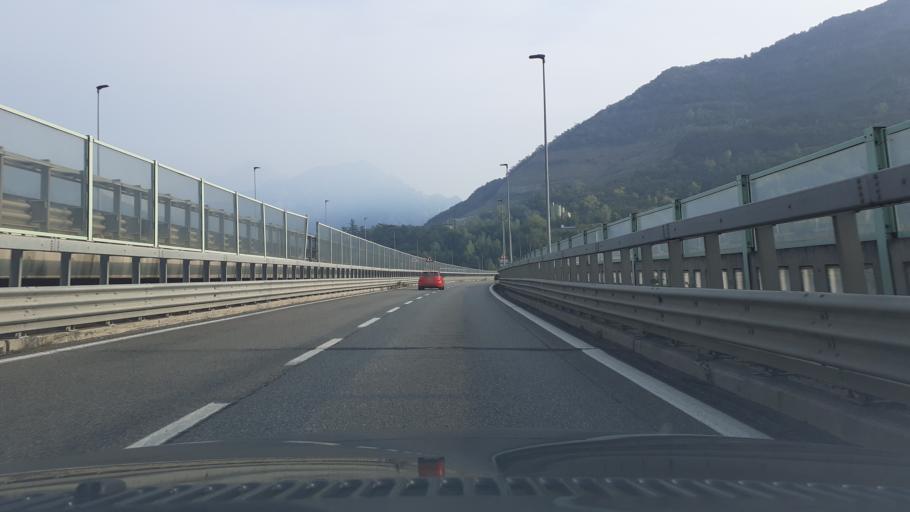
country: IT
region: Lombardy
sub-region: Provincia di Lecco
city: Civate
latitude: 45.8272
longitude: 9.3512
